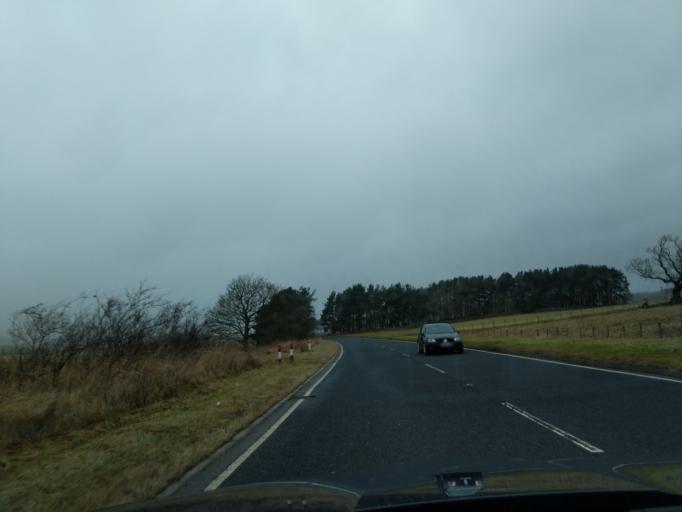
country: GB
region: England
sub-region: Northumberland
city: Otterburn
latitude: 55.2349
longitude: -2.1930
